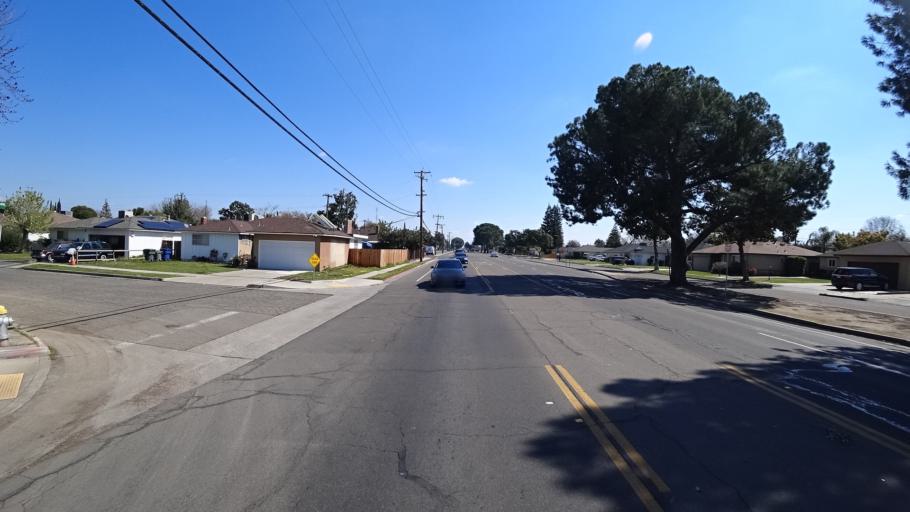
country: US
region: California
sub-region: Fresno County
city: Fresno
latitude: 36.8014
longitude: -119.7670
